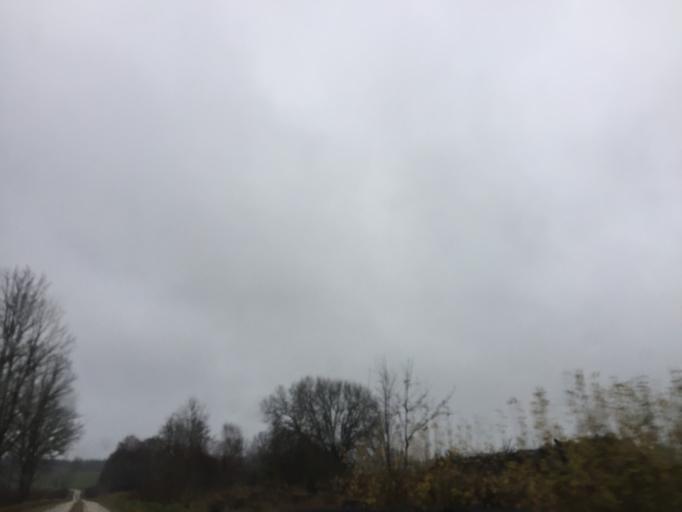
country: LV
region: Viesite
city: Viesite
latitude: 56.4487
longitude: 25.6294
